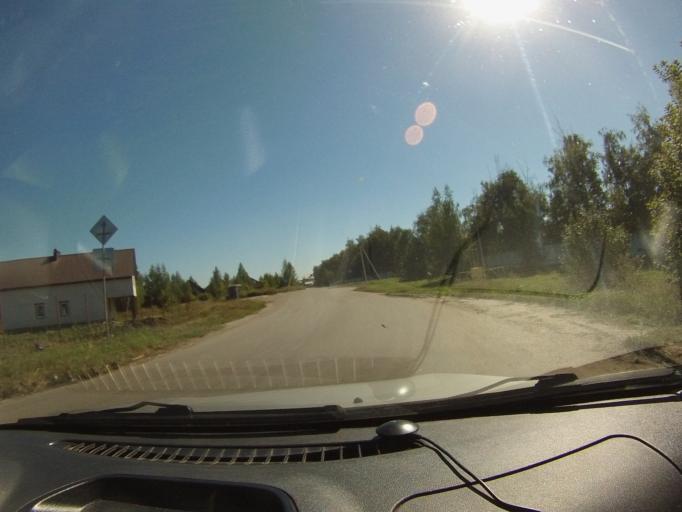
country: RU
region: Tambov
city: Komsomolets
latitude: 52.7685
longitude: 41.3615
